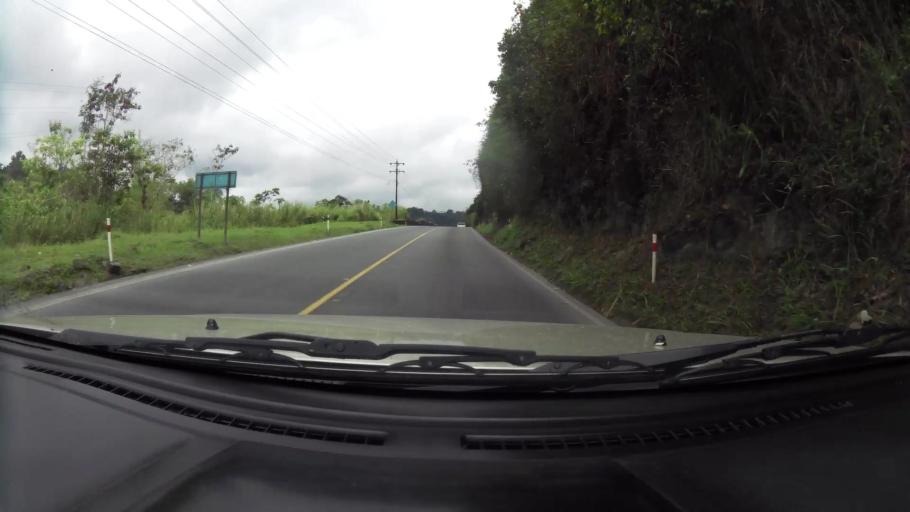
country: EC
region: Santo Domingo de los Tsachilas
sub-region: Canton Santo Domingo de los Colorados
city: Santo Domingo de los Colorados
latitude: -0.3066
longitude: -79.0417
